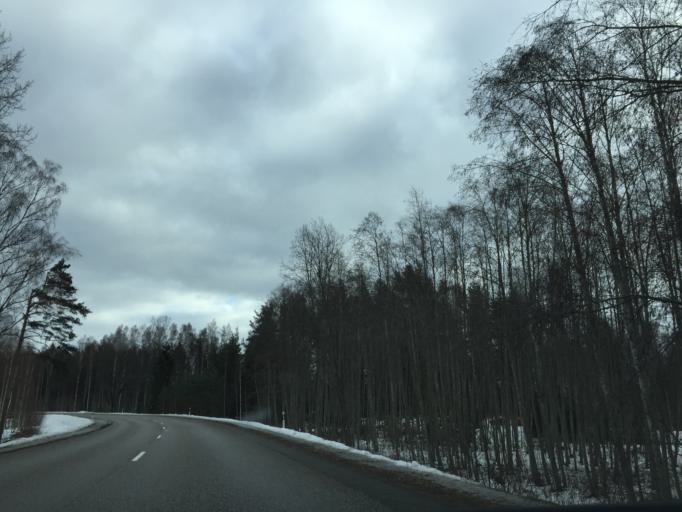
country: LV
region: Salacgrivas
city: Ainazi
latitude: 57.8562
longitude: 24.5155
